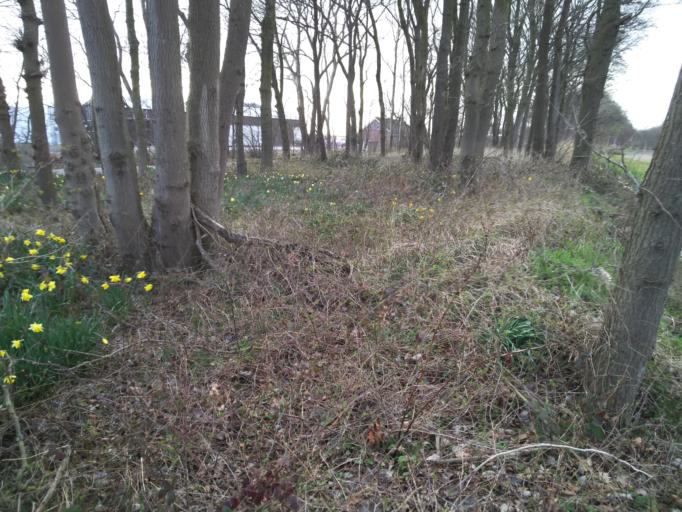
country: NL
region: South Holland
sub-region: Gemeente Teylingen
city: Sassenheim
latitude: 52.2490
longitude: 4.5303
